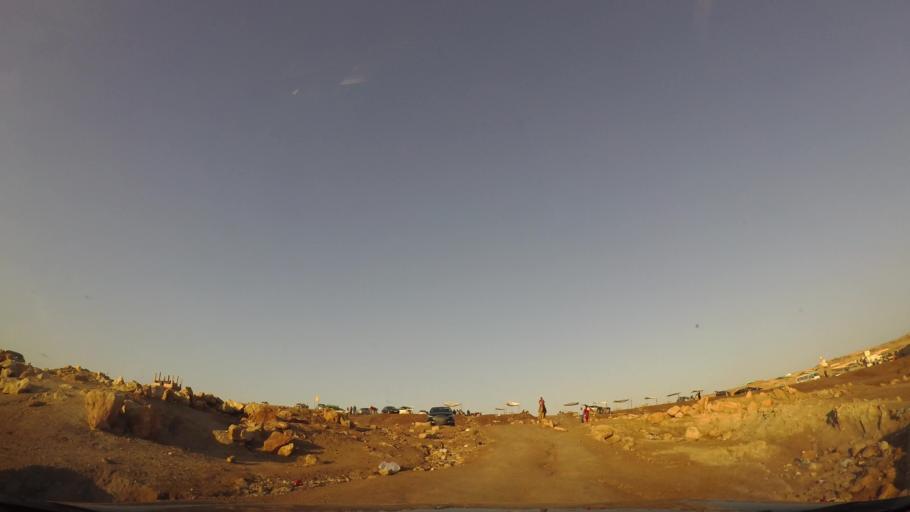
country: PS
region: West Bank
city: Jericho
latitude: 31.7475
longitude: 35.5905
